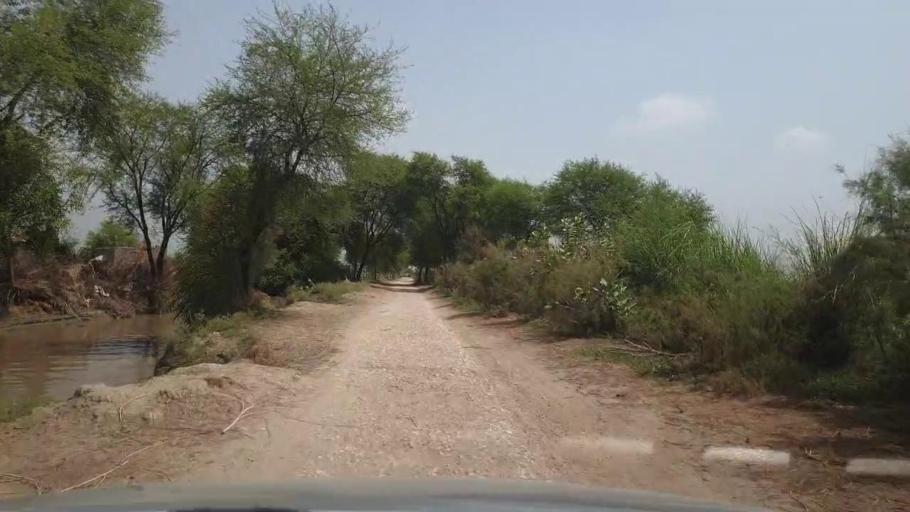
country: PK
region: Sindh
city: Garhi Yasin
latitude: 27.9365
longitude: 68.3674
